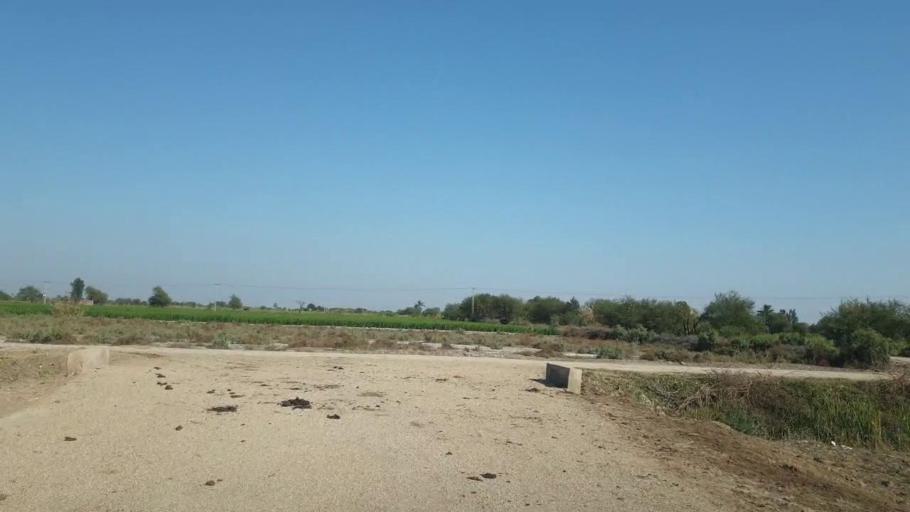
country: PK
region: Sindh
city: Mirpur Khas
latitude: 25.6274
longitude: 69.0435
